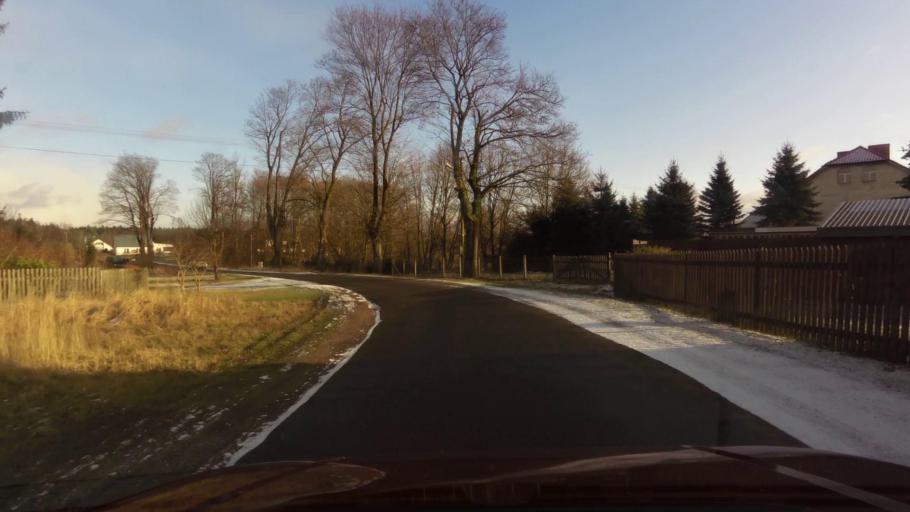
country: PL
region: West Pomeranian Voivodeship
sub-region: Powiat bialogardzki
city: Bialogard
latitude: 54.0940
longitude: 16.0571
